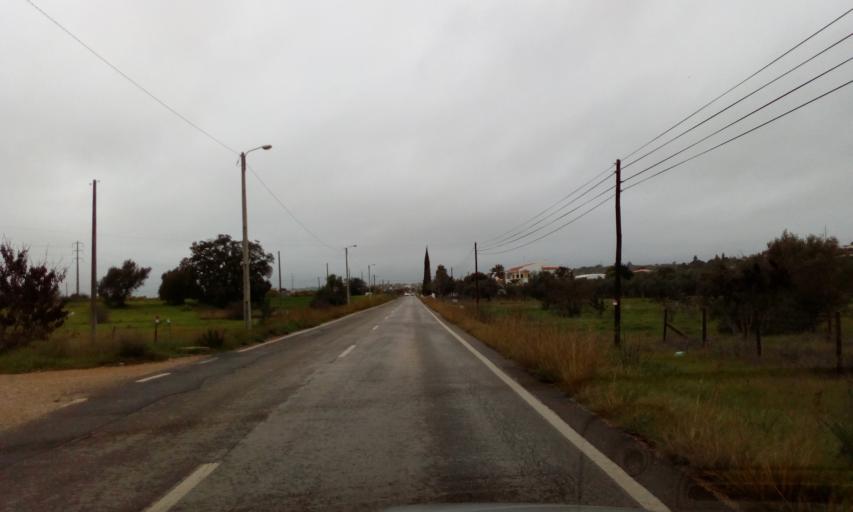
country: PT
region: Faro
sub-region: Albufeira
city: Guia
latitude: 37.1694
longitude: -8.3188
